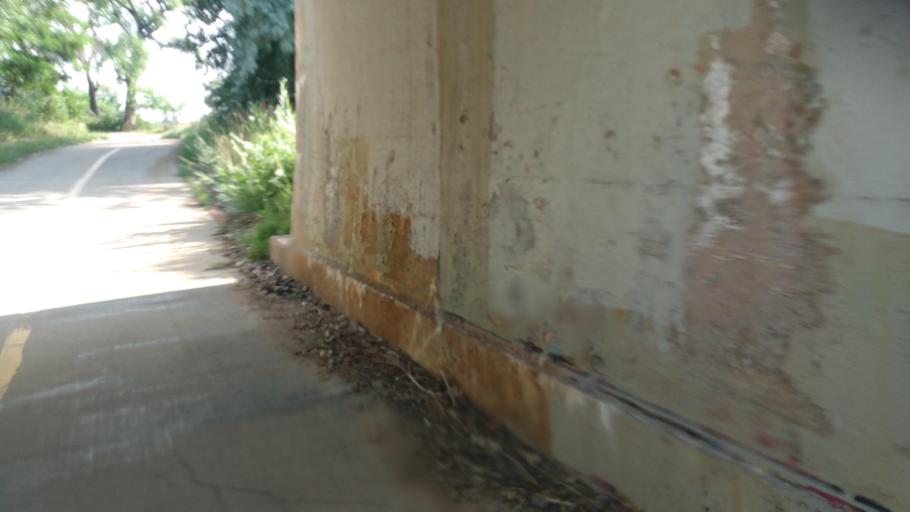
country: US
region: Colorado
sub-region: Boulder County
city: Boulder
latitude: 40.0176
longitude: -105.2159
